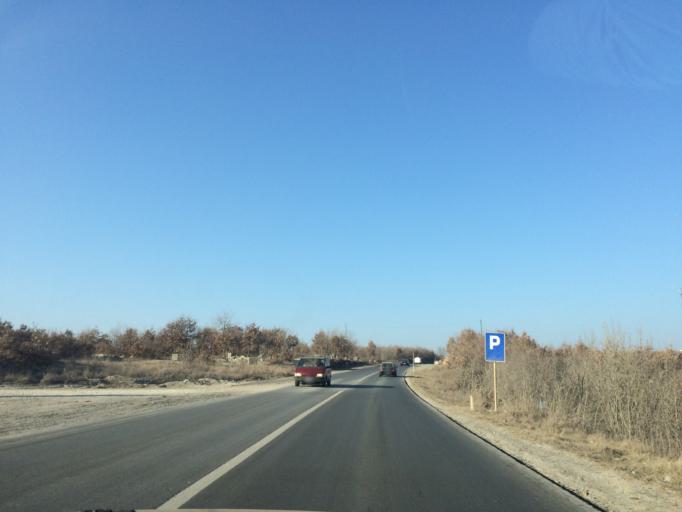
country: XK
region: Pec
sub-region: Komuna e Klines
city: Klina
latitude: 42.5940
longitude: 20.6349
